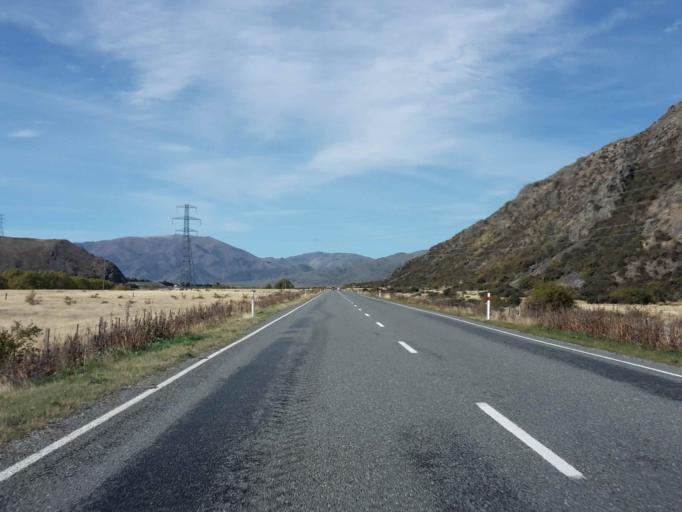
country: NZ
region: Otago
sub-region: Queenstown-Lakes District
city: Wanaka
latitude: -44.5013
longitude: 169.7693
